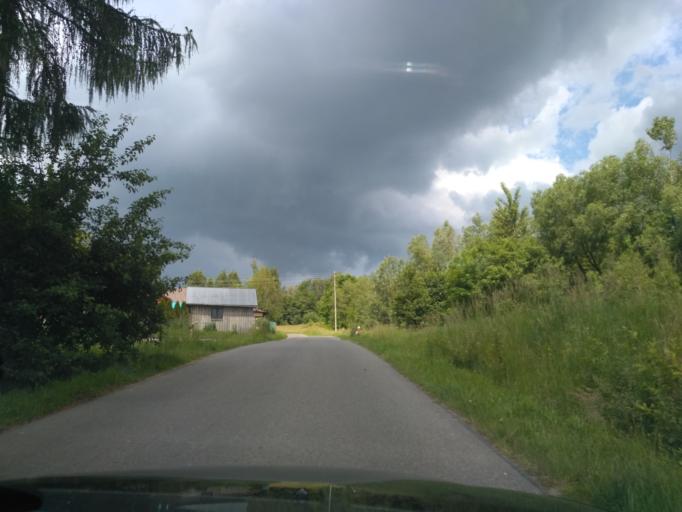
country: PL
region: Subcarpathian Voivodeship
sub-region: Powiat rzeszowski
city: Hyzne
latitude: 49.9348
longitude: 22.1711
